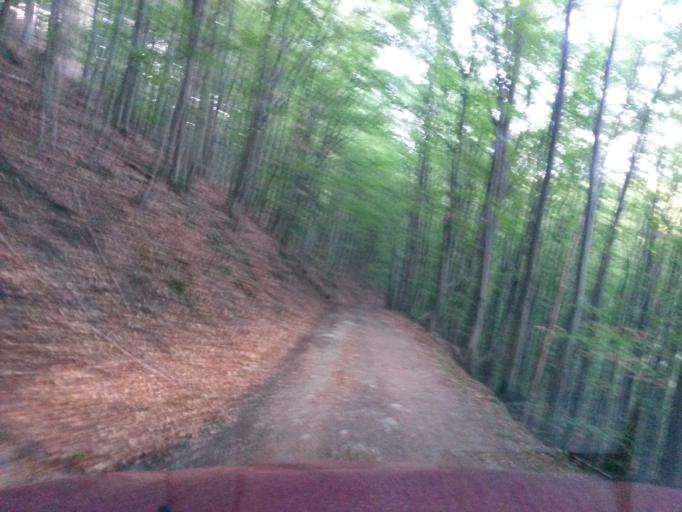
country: SK
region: Kosicky
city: Moldava nad Bodvou
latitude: 48.7339
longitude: 21.0637
